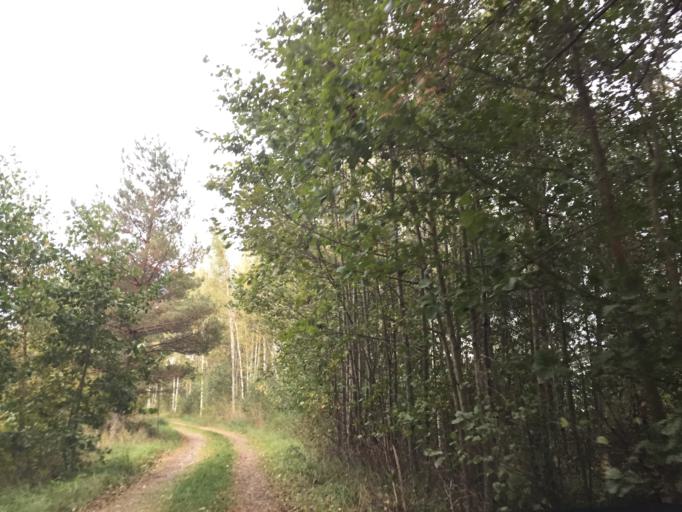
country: LV
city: Tireli
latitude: 56.8971
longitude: 23.5178
